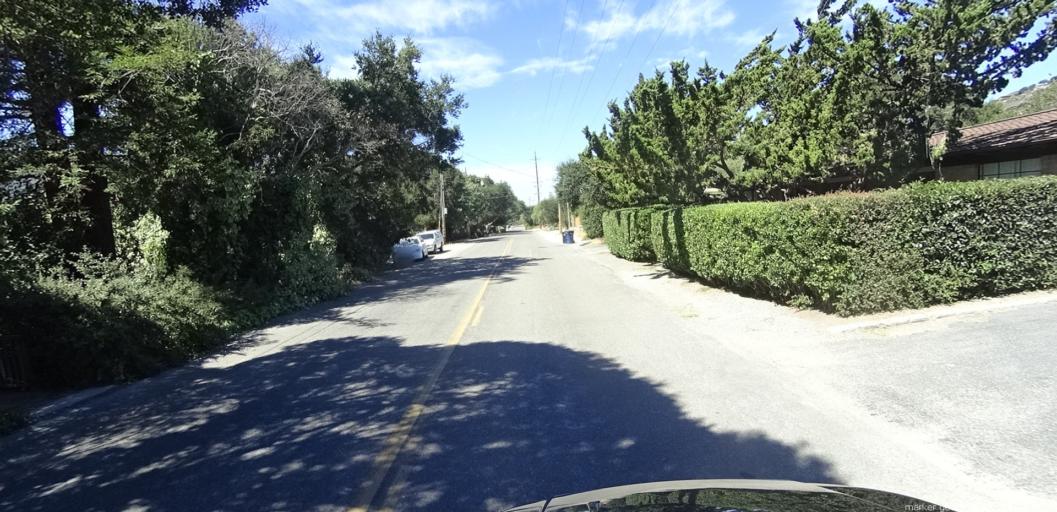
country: US
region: California
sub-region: Monterey County
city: Carmel Valley Village
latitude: 36.4806
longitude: -121.7292
